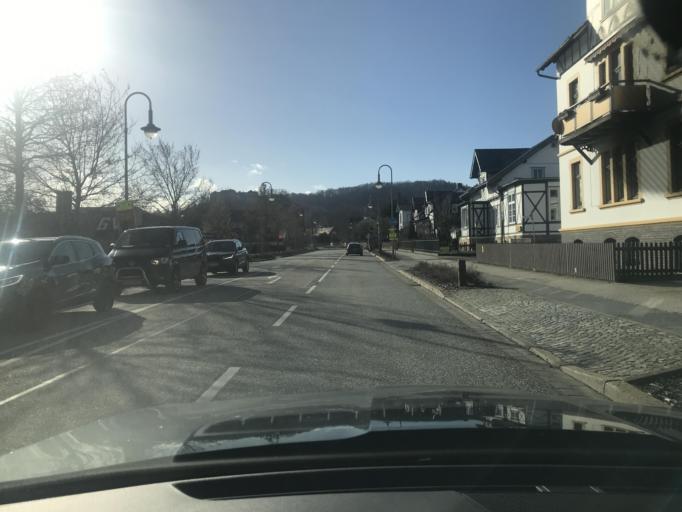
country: DE
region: Saxony-Anhalt
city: Blankenburg
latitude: 51.7956
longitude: 10.9514
